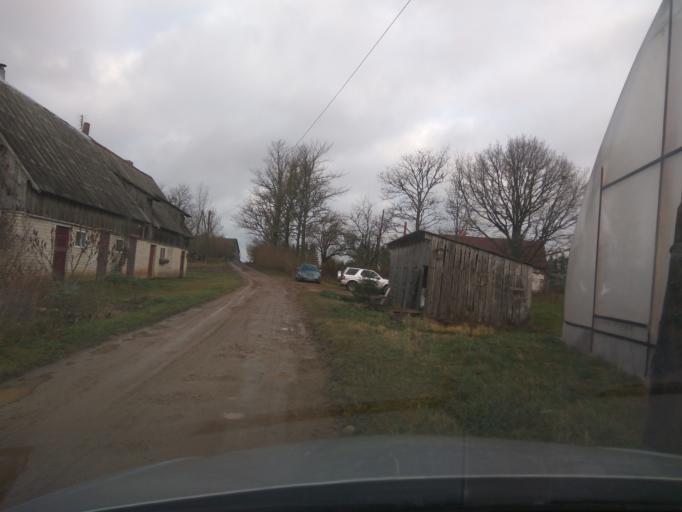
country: LV
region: Skrunda
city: Skrunda
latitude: 56.8445
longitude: 22.2214
